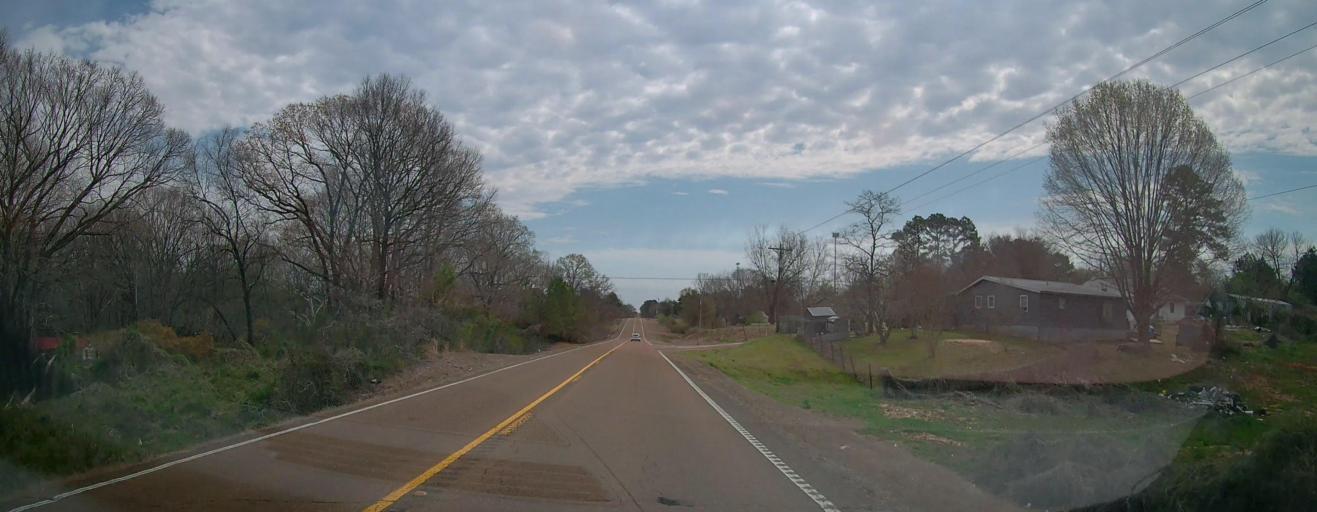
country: US
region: Mississippi
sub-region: Marshall County
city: Holly Springs
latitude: 34.8230
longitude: -89.5496
